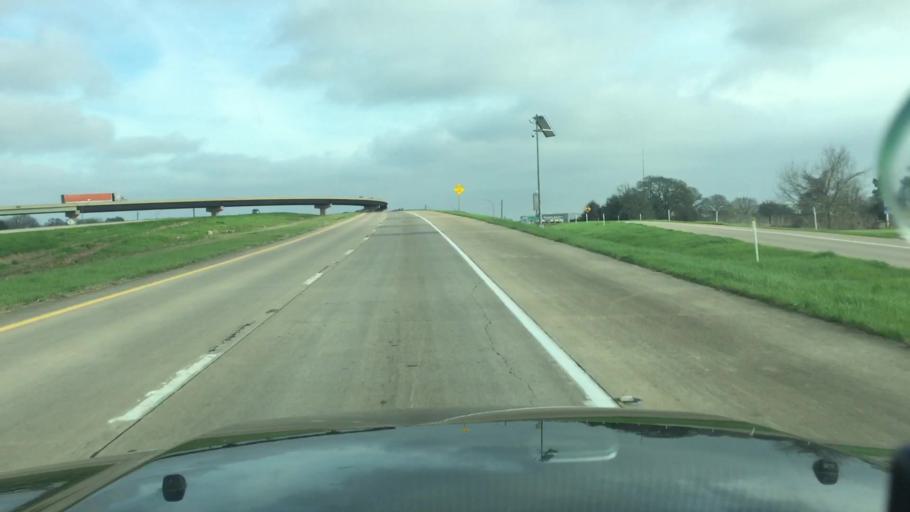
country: US
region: Texas
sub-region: Waller County
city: Hempstead
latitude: 30.1149
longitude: -96.0792
